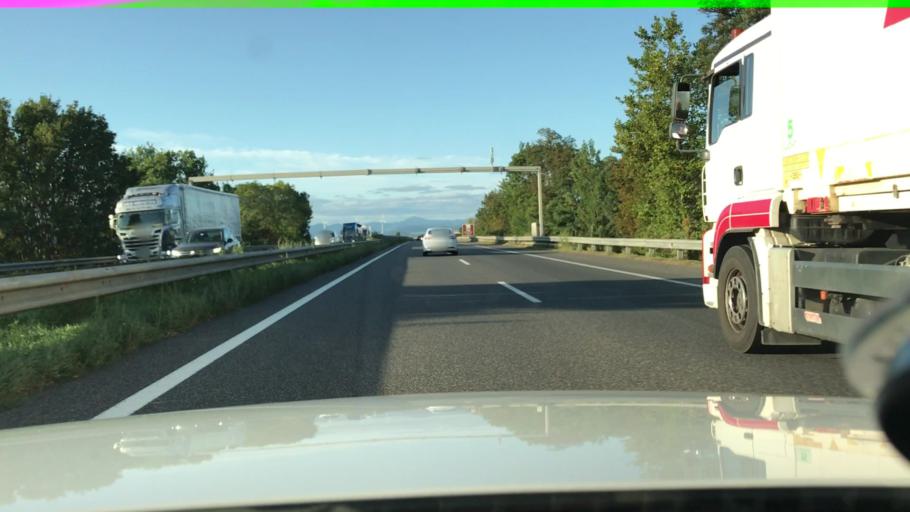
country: AT
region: Lower Austria
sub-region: Sankt Polten Stadt
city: Sankt Poelten
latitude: 48.2180
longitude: 15.6749
